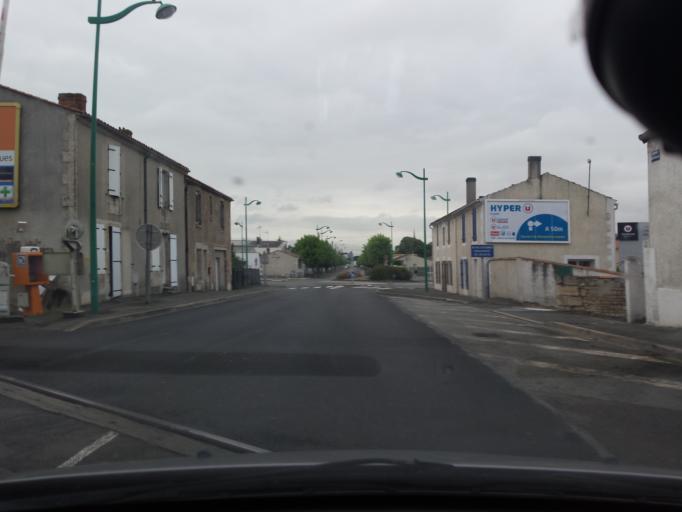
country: FR
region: Pays de la Loire
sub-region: Departement de la Vendee
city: Lucon
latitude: 46.4646
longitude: -1.1723
